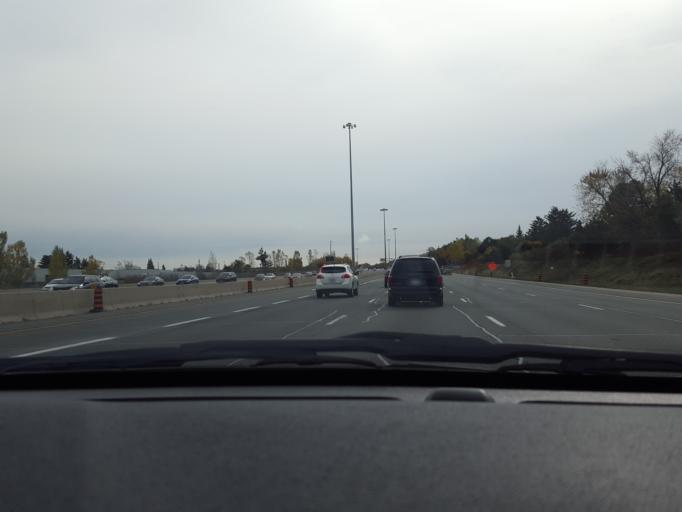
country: CA
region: Ontario
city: Willowdale
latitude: 43.8235
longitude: -79.3622
